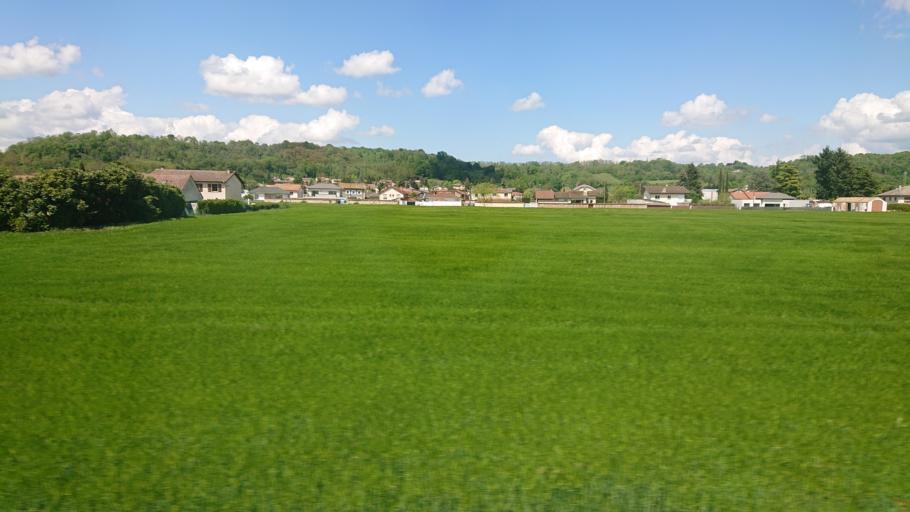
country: FR
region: Rhone-Alpes
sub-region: Departement de l'Ain
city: Dagneux
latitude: 45.8487
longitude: 5.0824
